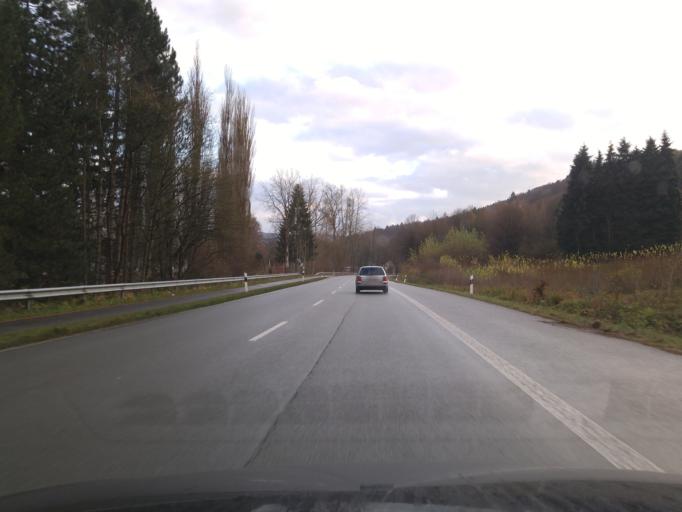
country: DE
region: Lower Saxony
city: Hannoversch Munden
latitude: 51.4315
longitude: 9.6346
